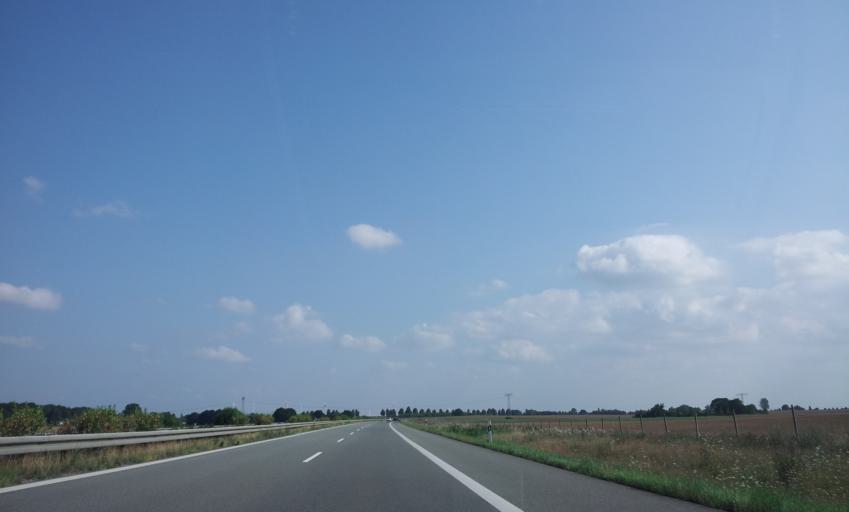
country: DE
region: Mecklenburg-Vorpommern
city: Dersekow
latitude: 54.0310
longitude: 13.2756
